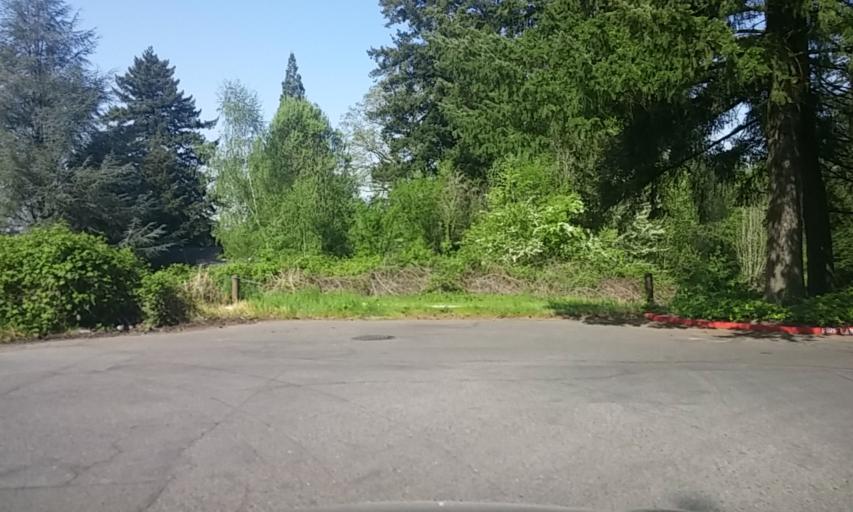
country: US
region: Oregon
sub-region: Washington County
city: Metzger
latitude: 45.4369
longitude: -122.7476
